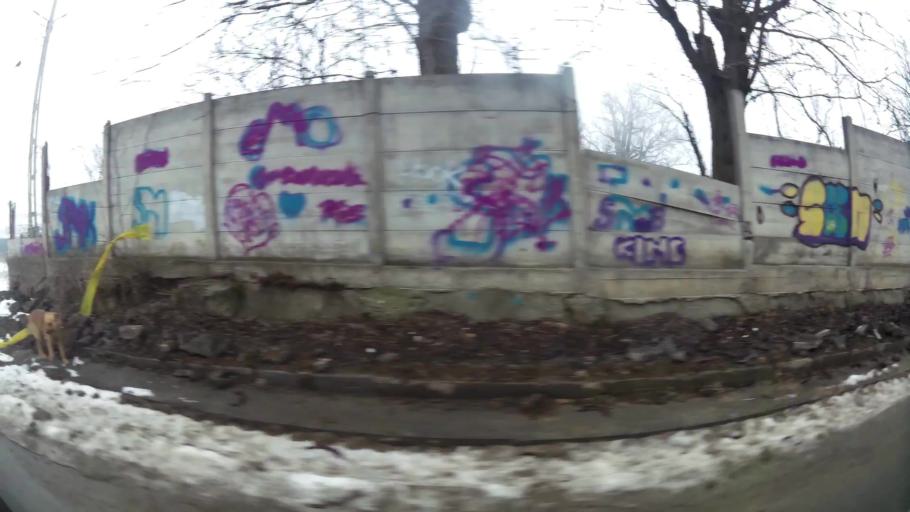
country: RO
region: Ilfov
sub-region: Comuna Chiajna
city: Chiajna
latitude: 44.4597
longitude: 25.9889
